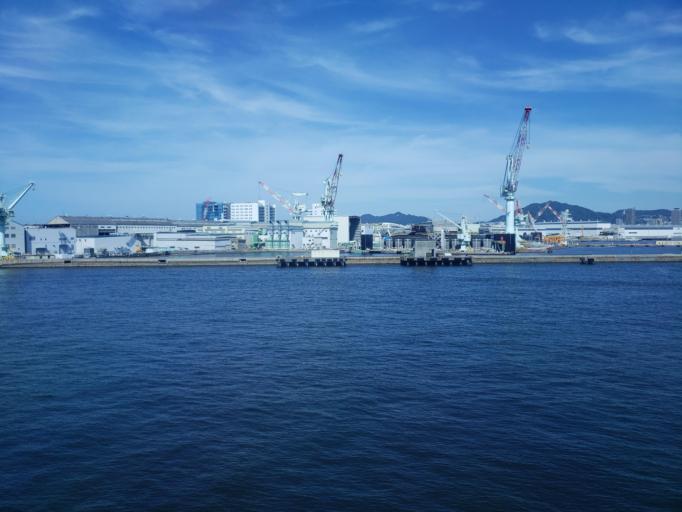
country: JP
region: Hyogo
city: Kobe
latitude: 34.6545
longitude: 135.1886
